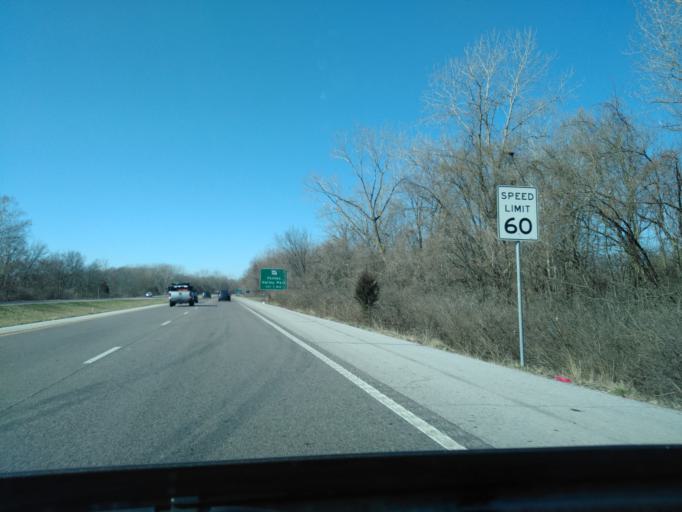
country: US
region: Missouri
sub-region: Saint Louis County
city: Fenton
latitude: 38.5189
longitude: -90.4217
